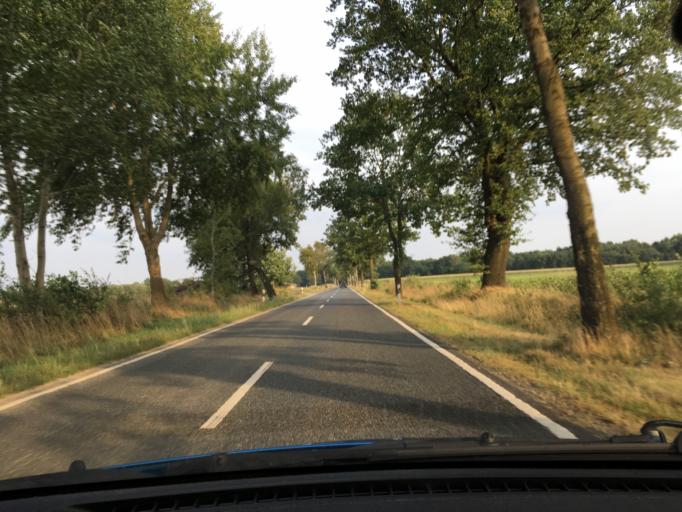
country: DE
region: Lower Saxony
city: Toppenstedt
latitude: 53.3059
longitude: 10.0847
